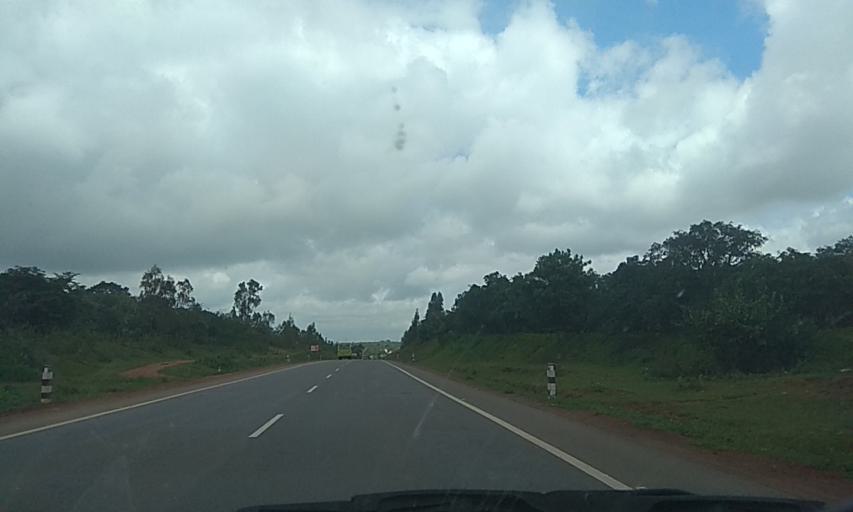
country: IN
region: Karnataka
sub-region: Dharwad
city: Hubli
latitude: 15.4479
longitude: 74.9687
